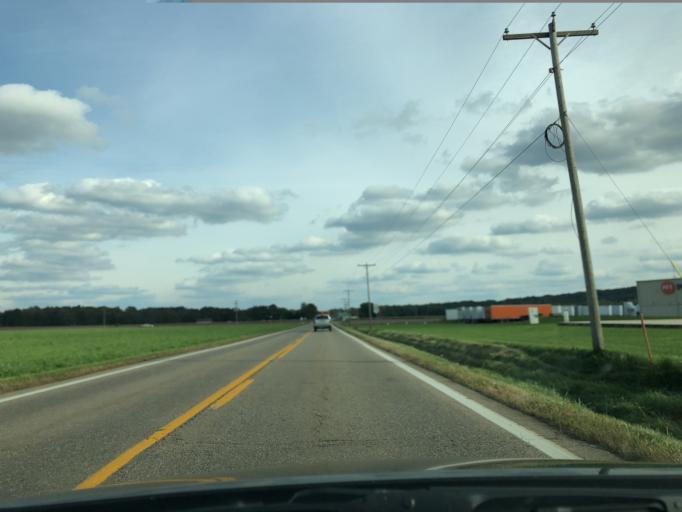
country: US
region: Ohio
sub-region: Stark County
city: Beach City
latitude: 40.6422
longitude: -81.5815
